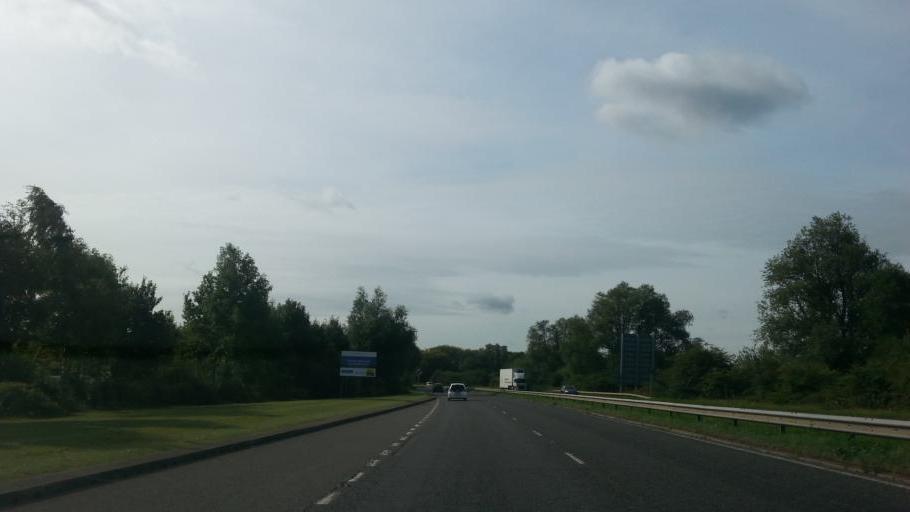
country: GB
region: England
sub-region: Leicestershire
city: Syston
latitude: 52.6912
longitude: -1.0972
